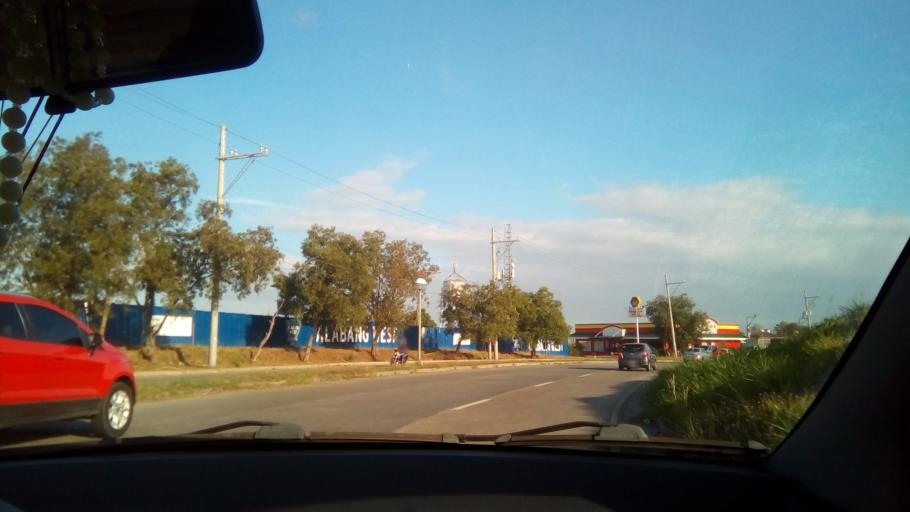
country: PH
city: Sambayanihan People's Village
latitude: 14.4056
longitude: 121.0120
